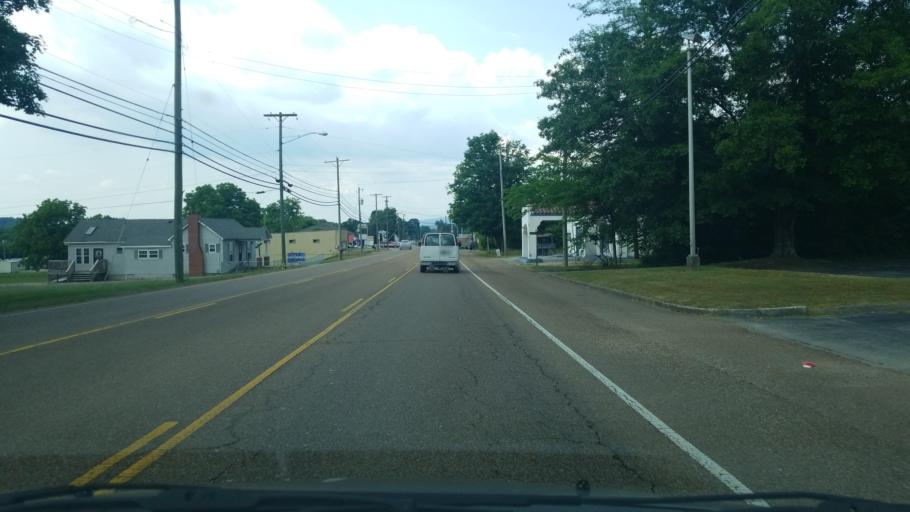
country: US
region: Tennessee
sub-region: Hamilton County
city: Soddy-Daisy
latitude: 35.2455
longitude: -85.1886
